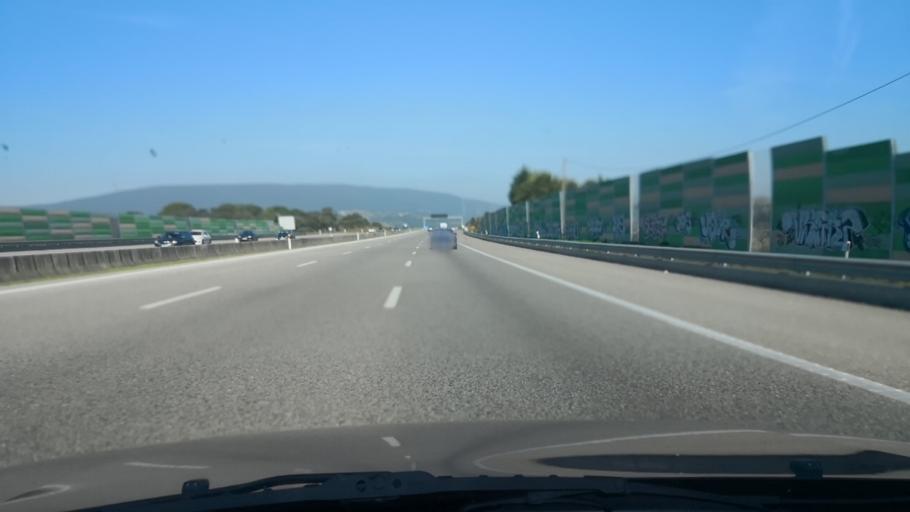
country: PT
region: Santarem
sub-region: Alcanena
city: Alcanena
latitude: 39.4560
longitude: -8.6310
